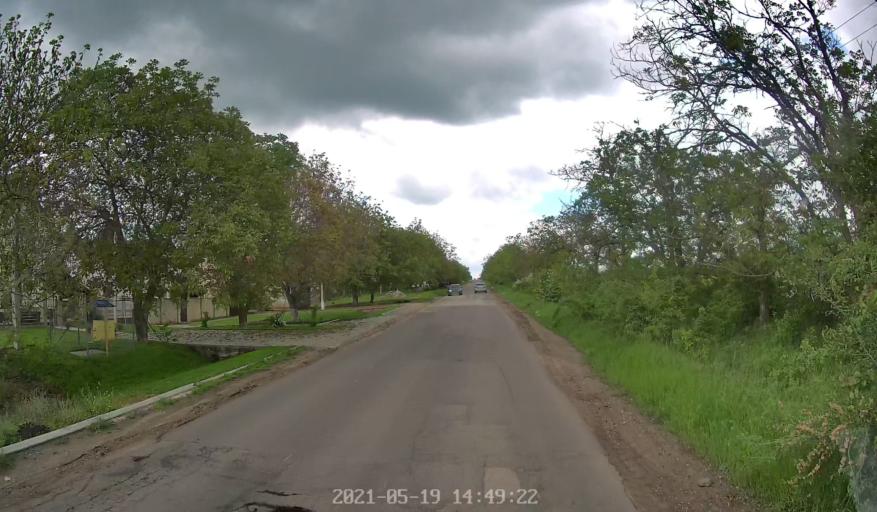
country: MD
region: Chisinau
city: Stauceni
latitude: 47.0494
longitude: 28.9521
